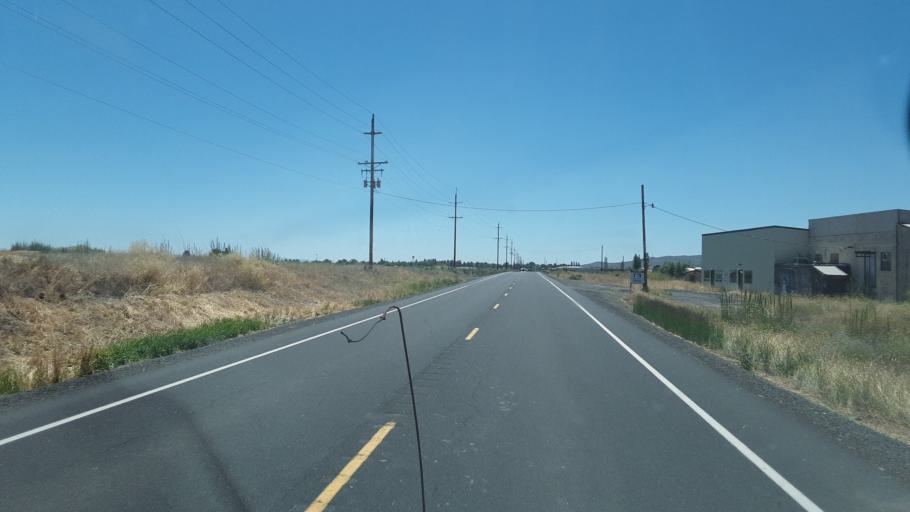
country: US
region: California
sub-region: Siskiyou County
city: Tulelake
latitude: 42.0380
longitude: -121.6214
